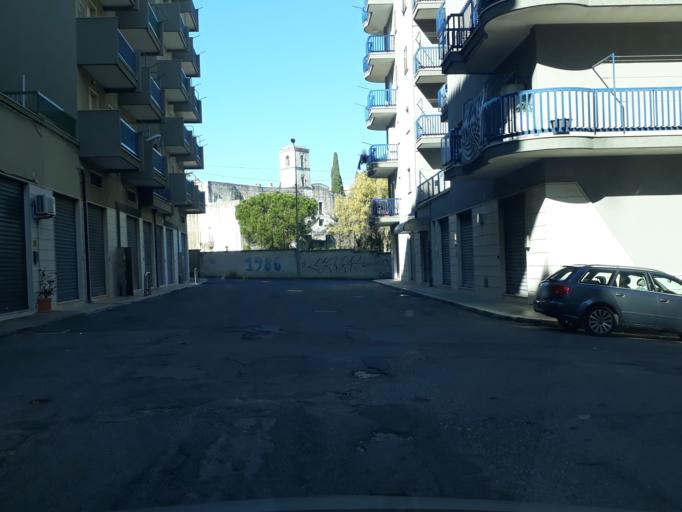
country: IT
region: Apulia
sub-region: Provincia di Taranto
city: Martina Franca
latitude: 40.7043
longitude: 17.3461
